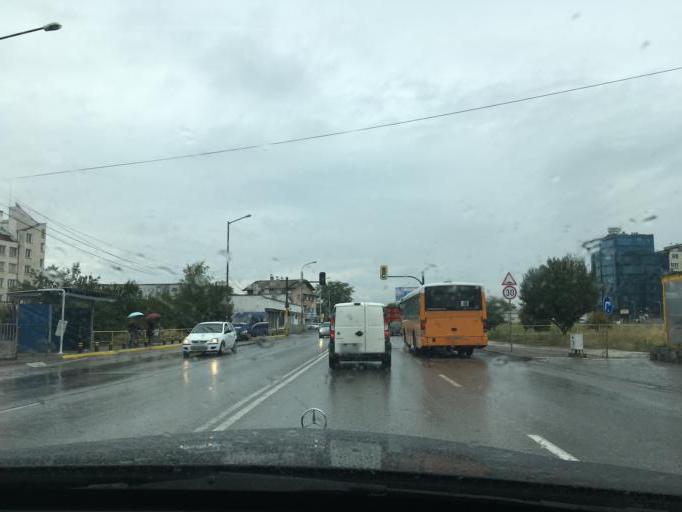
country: BG
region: Sofiya
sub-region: Obshtina Bozhurishte
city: Bozhurishte
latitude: 42.7324
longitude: 23.2523
